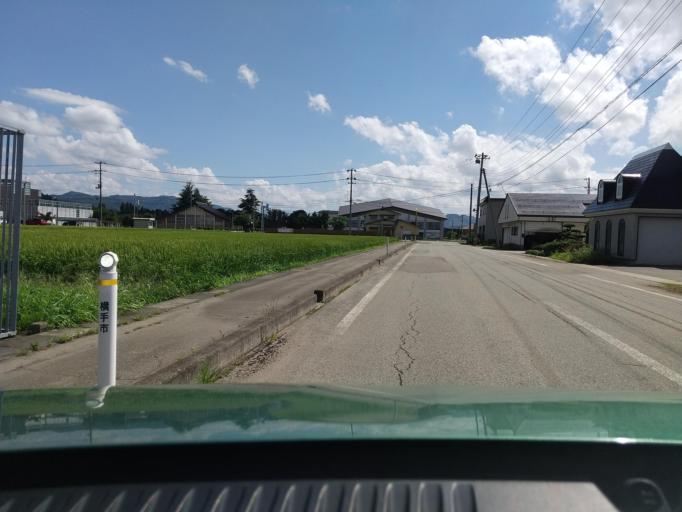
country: JP
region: Akita
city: Yuzawa
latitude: 39.2045
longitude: 140.5565
